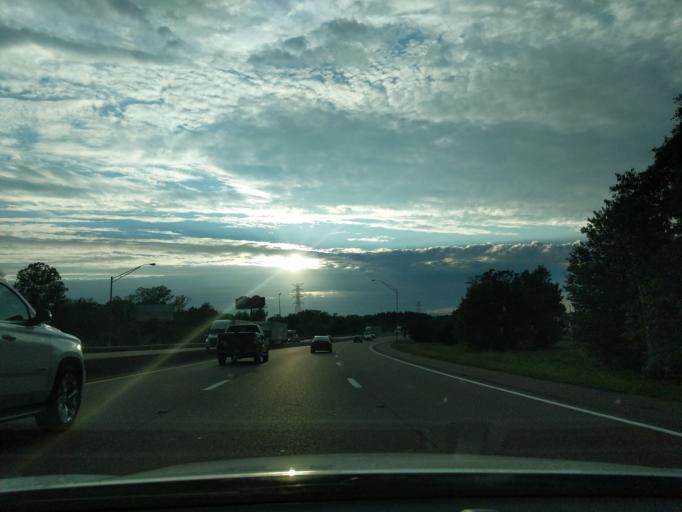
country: US
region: Tennessee
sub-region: Shelby County
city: New South Memphis
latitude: 35.0796
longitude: -90.0684
